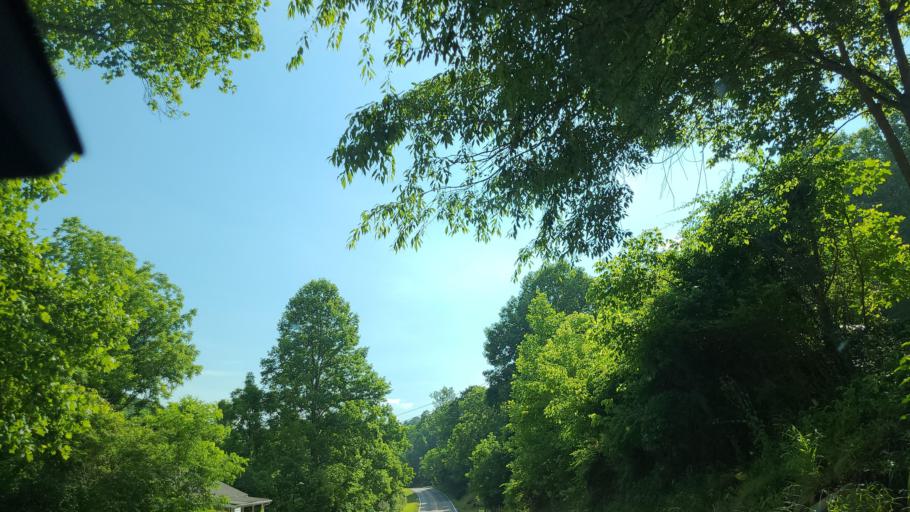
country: US
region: Kentucky
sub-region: Bell County
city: Pineville
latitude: 36.7102
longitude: -83.8252
